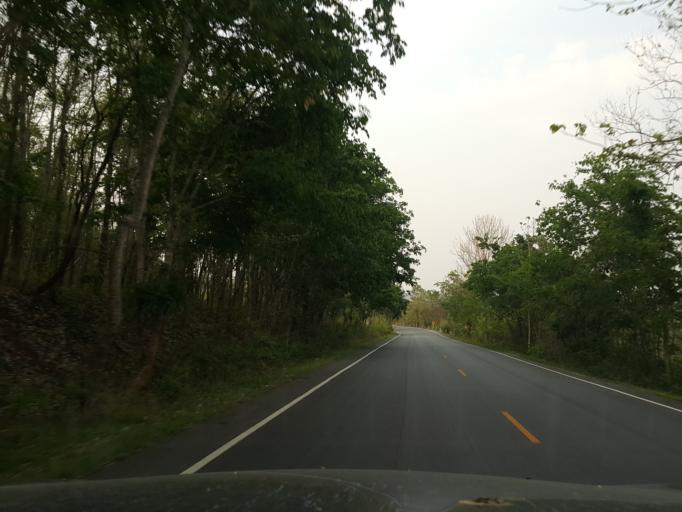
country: TH
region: Lamphun
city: Li
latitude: 17.8518
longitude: 99.0234
